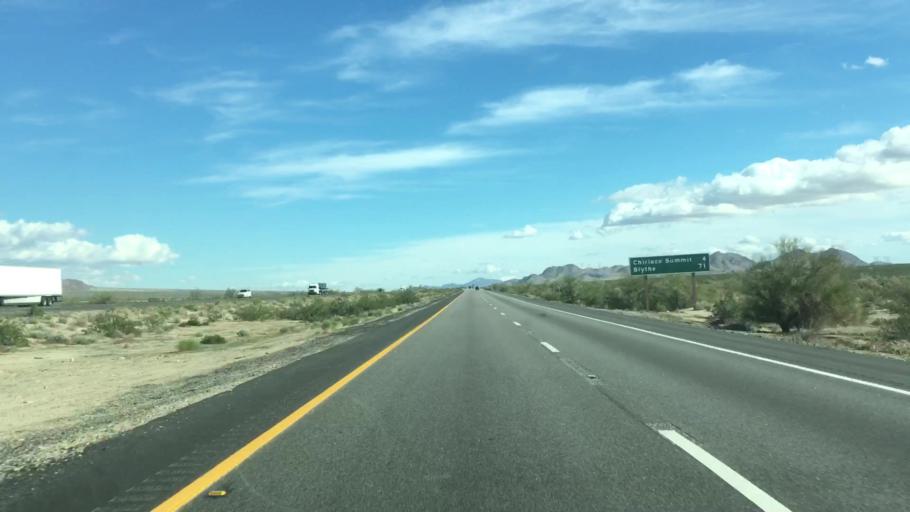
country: US
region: California
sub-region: Riverside County
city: Mecca
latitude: 33.6600
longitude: -115.7893
